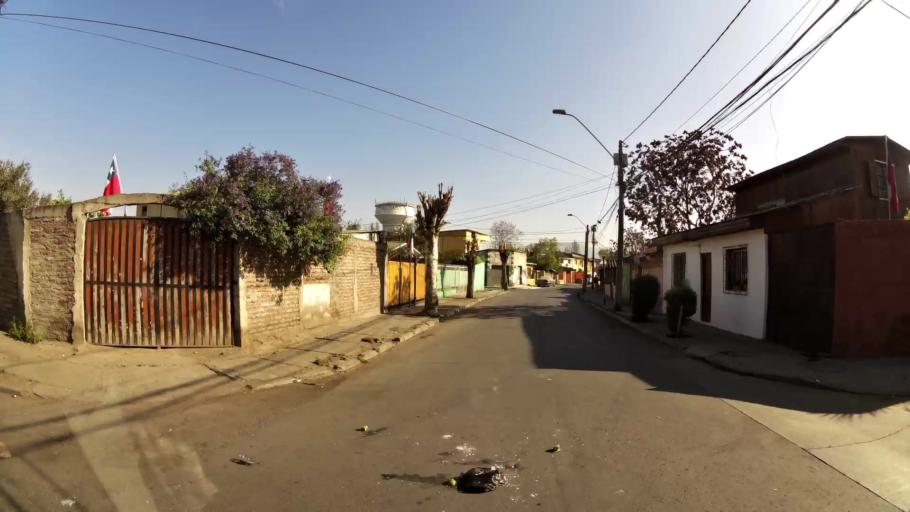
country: CL
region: Santiago Metropolitan
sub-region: Provincia de Santiago
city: Santiago
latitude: -33.3803
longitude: -70.6743
